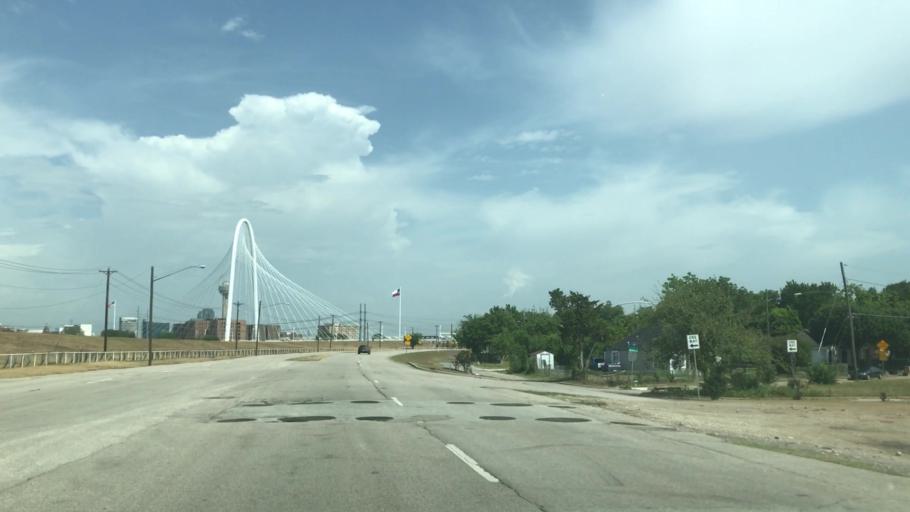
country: US
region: Texas
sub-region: Dallas County
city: Dallas
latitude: 32.7834
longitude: -96.8306
